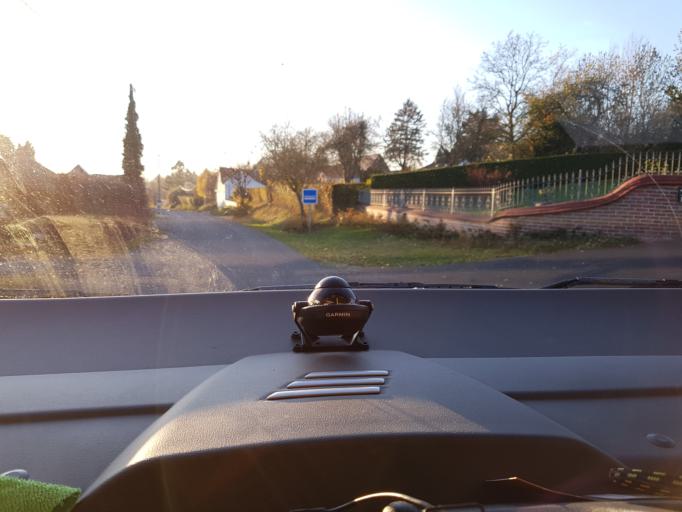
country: FR
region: Nord-Pas-de-Calais
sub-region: Departement du Pas-de-Calais
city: Beaurainville
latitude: 50.5143
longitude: 1.9348
